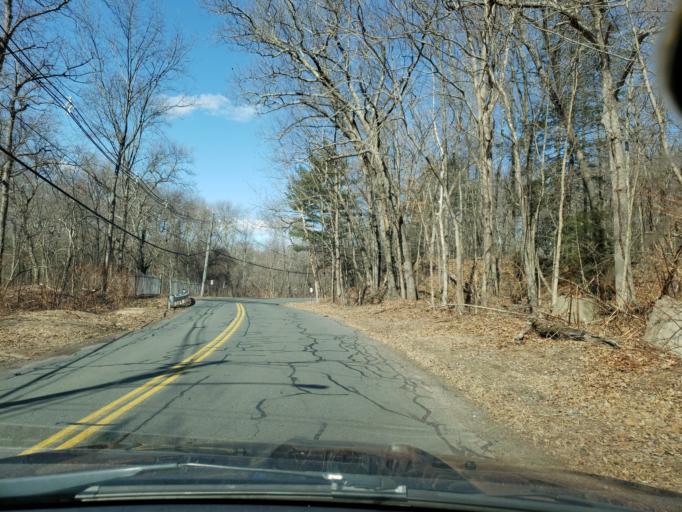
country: US
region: Connecticut
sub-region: Hartford County
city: Hazardville
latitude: 41.9779
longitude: -72.5408
